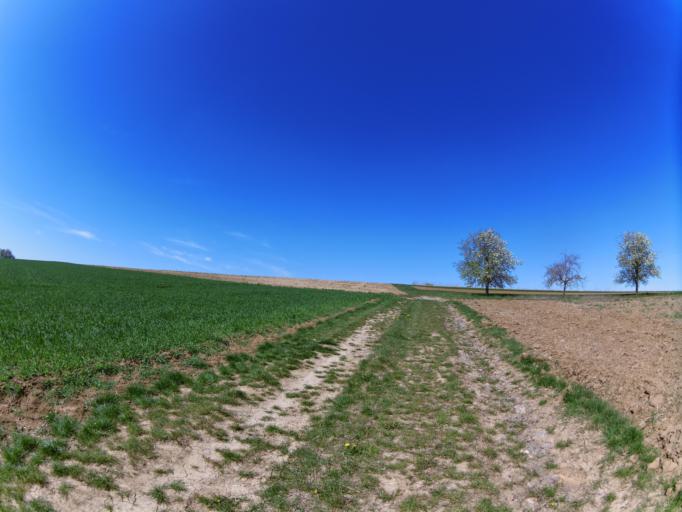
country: DE
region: Bavaria
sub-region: Regierungsbezirk Unterfranken
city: Winterhausen
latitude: 49.6951
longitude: 9.9926
